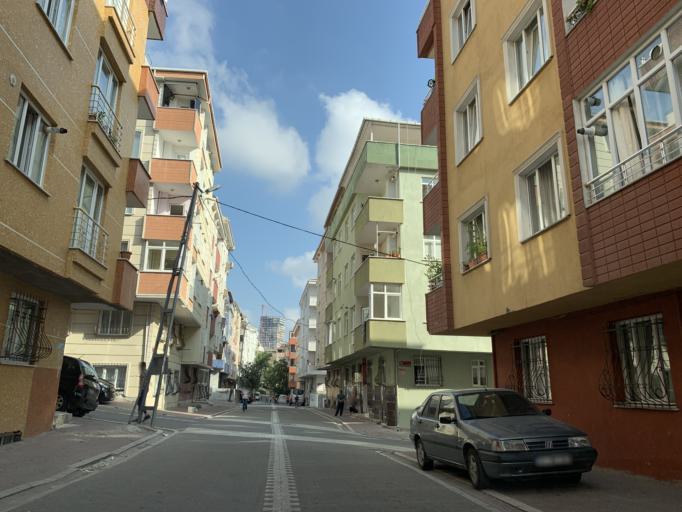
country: TR
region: Istanbul
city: Esenyurt
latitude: 41.0282
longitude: 28.6791
